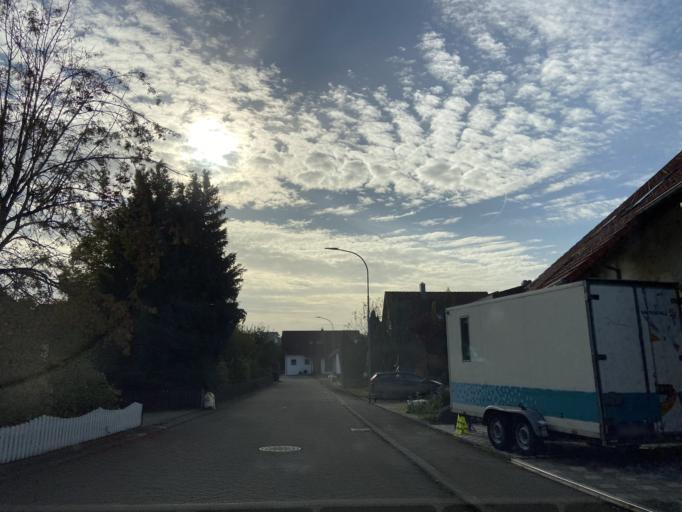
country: DE
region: Baden-Wuerttemberg
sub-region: Tuebingen Region
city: Bingen
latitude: 48.1116
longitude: 9.2679
